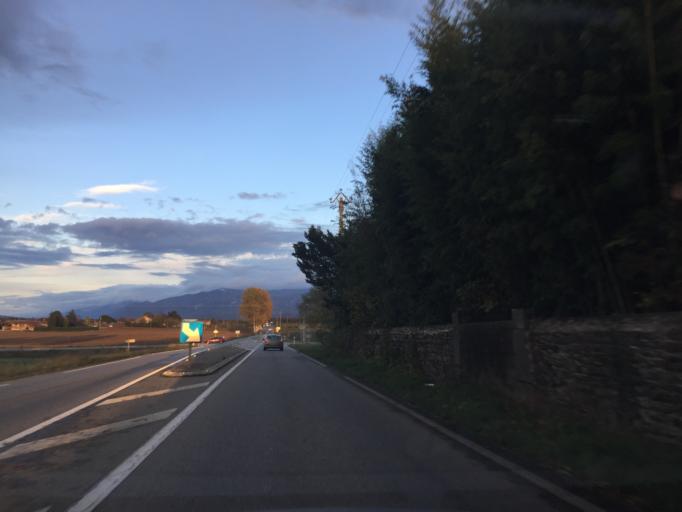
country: FR
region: Rhone-Alpes
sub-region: Departement de l'Isere
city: Saint-Lattier
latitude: 45.0565
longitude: 5.1955
